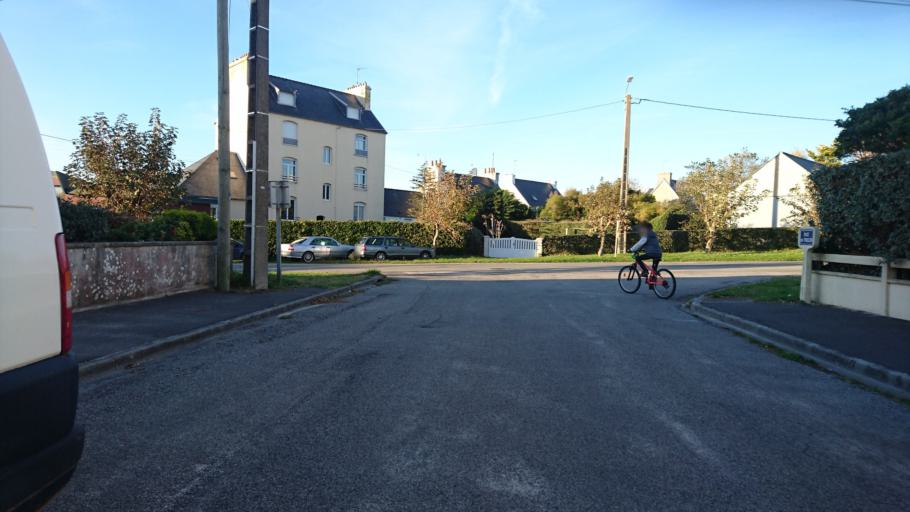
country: FR
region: Brittany
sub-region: Departement du Finistere
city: Lampaul-Plouarzel
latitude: 48.4455
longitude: -4.7729
